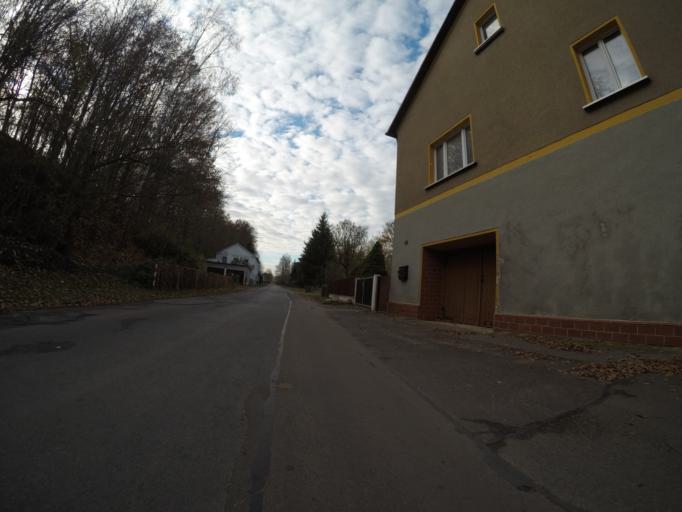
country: DE
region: Thuringia
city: Heyersdorf
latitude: 50.8573
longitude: 12.3769
